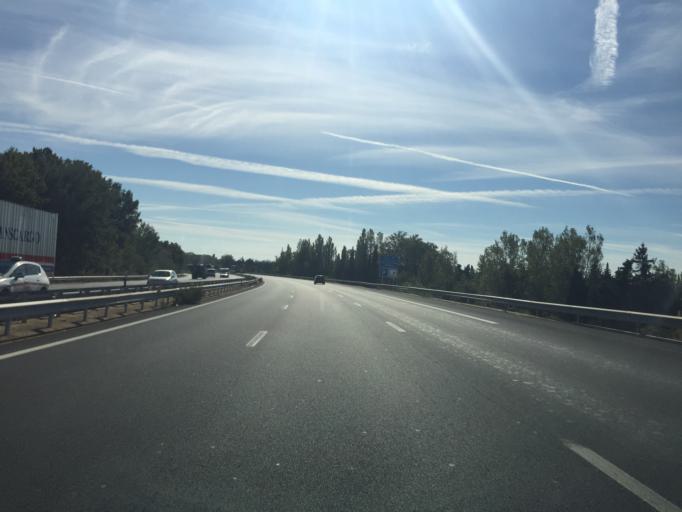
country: FR
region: Provence-Alpes-Cote d'Azur
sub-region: Departement des Bouches-du-Rhone
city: Noves
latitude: 43.8821
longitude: 4.9251
